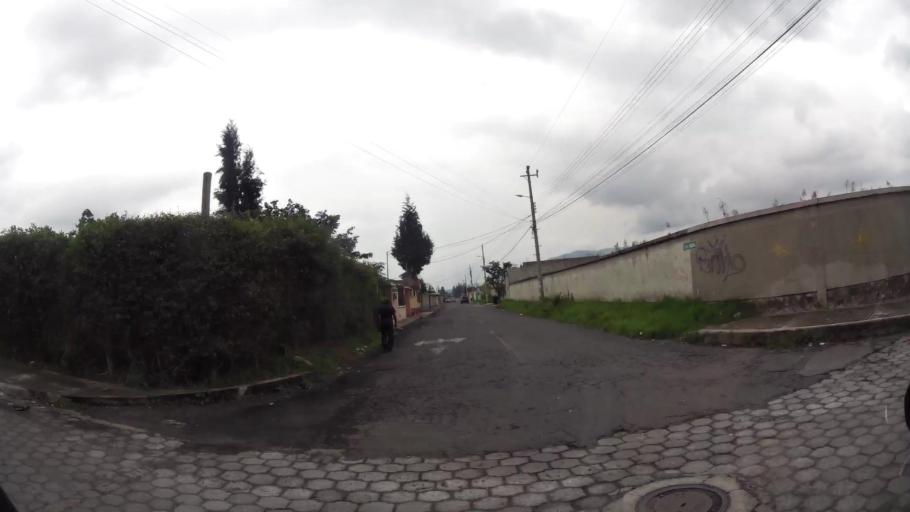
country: EC
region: Pichincha
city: Sangolqui
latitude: -0.3222
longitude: -78.4692
